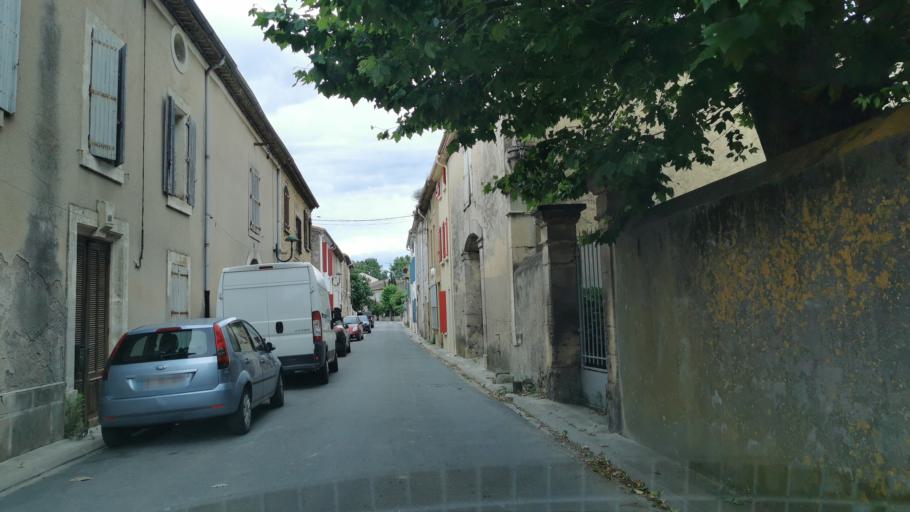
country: FR
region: Languedoc-Roussillon
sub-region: Departement de l'Aude
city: Moussan
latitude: 43.2311
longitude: 2.9487
